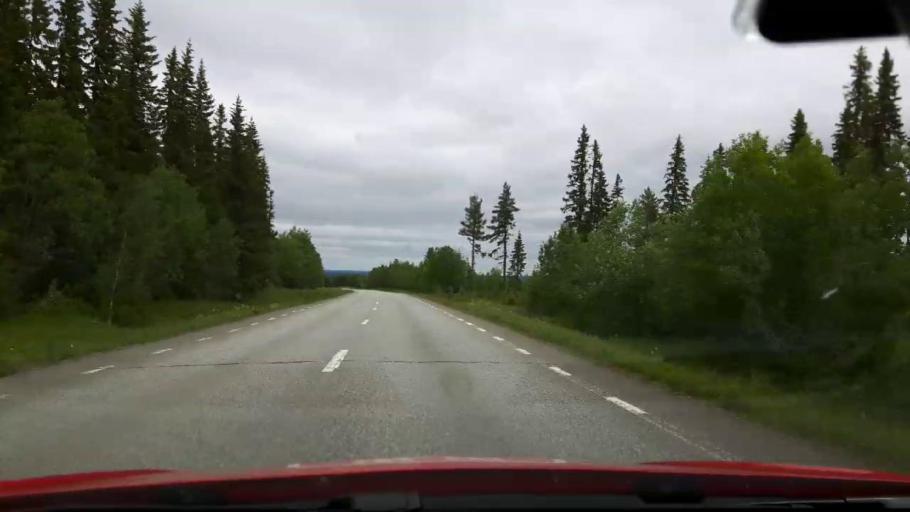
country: SE
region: Jaemtland
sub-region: Krokoms Kommun
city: Krokom
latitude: 63.5737
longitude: 14.6293
